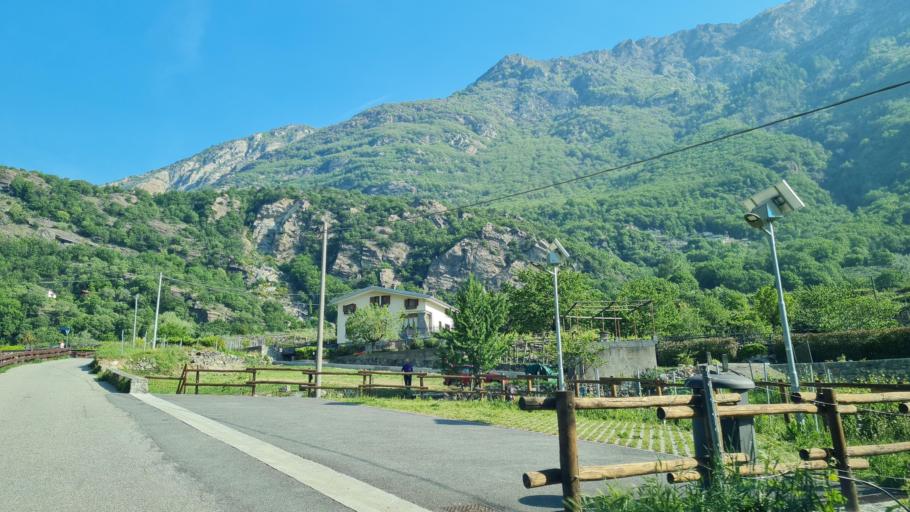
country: IT
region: Aosta Valley
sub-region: Valle d'Aosta
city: Donnas
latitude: 45.6045
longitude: 7.7652
